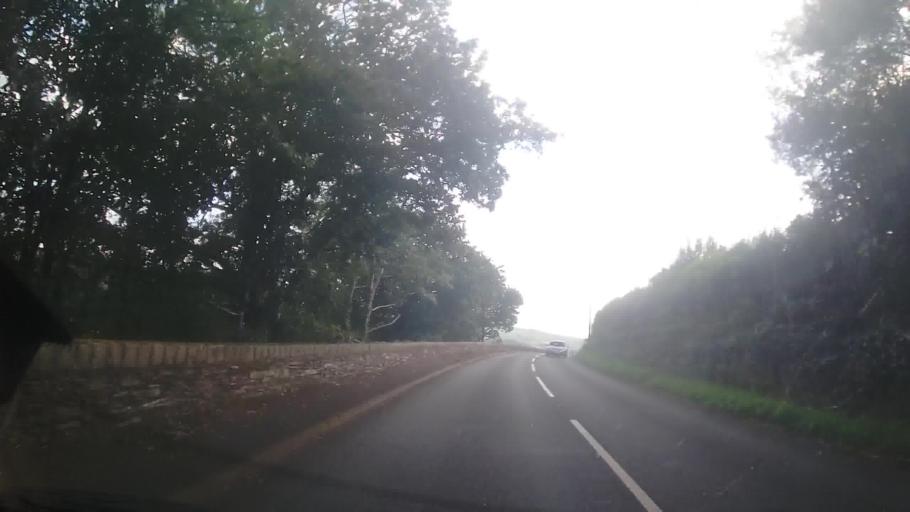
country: GB
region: Wales
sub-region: Gwynedd
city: Barmouth
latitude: 52.7262
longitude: -4.0316
